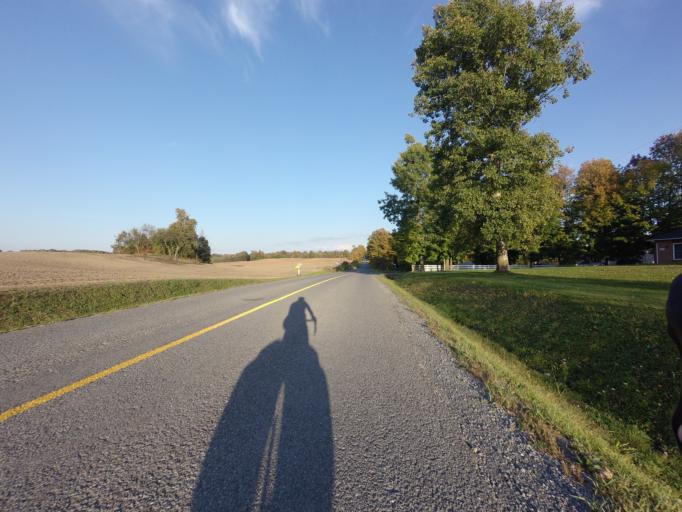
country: CA
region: Ontario
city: Kingston
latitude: 44.3788
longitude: -76.3599
